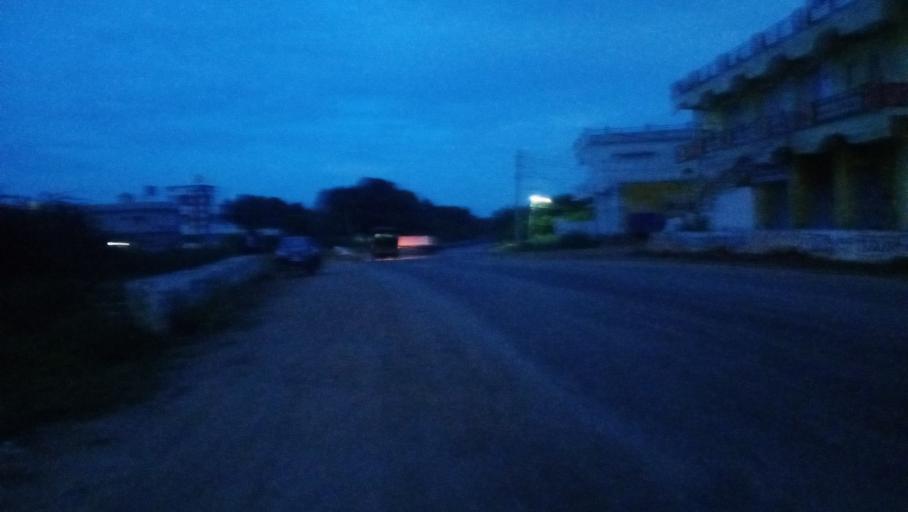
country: IN
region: Karnataka
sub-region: Tumkur
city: Pavagada
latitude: 13.9398
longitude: 77.2778
